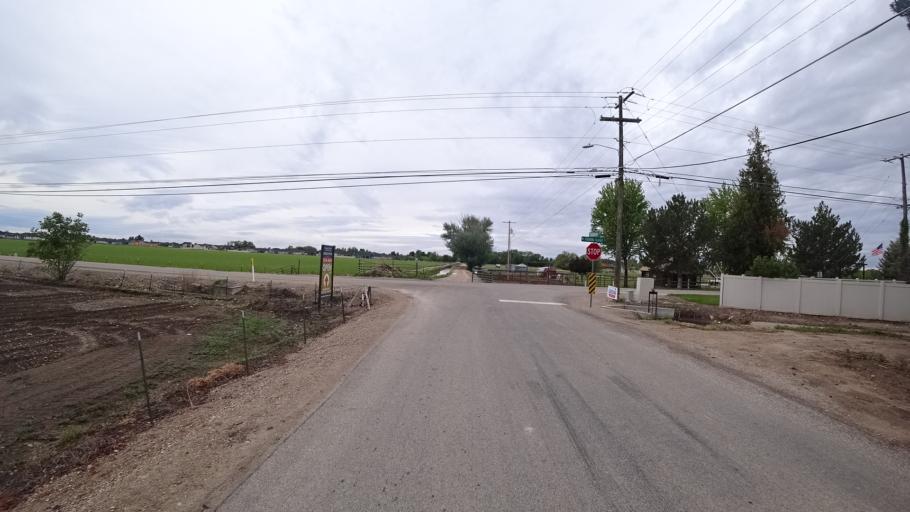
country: US
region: Idaho
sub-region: Ada County
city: Star
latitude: 43.7067
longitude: -116.4883
